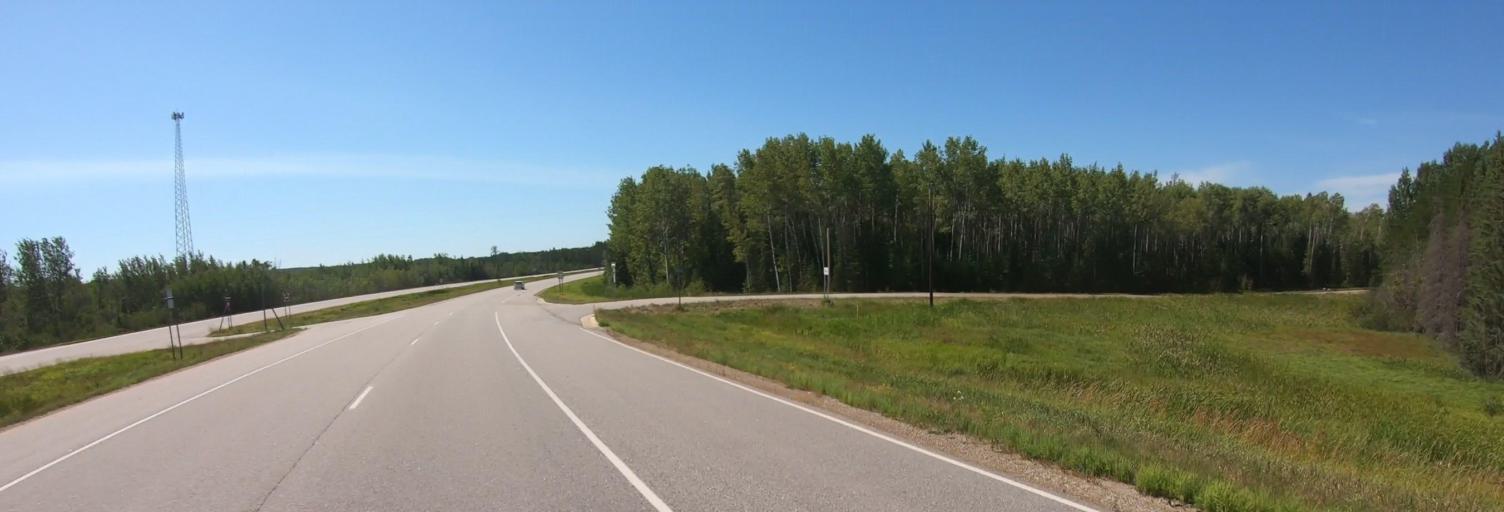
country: US
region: Minnesota
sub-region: Saint Louis County
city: Mountain Iron
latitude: 47.7451
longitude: -92.6473
